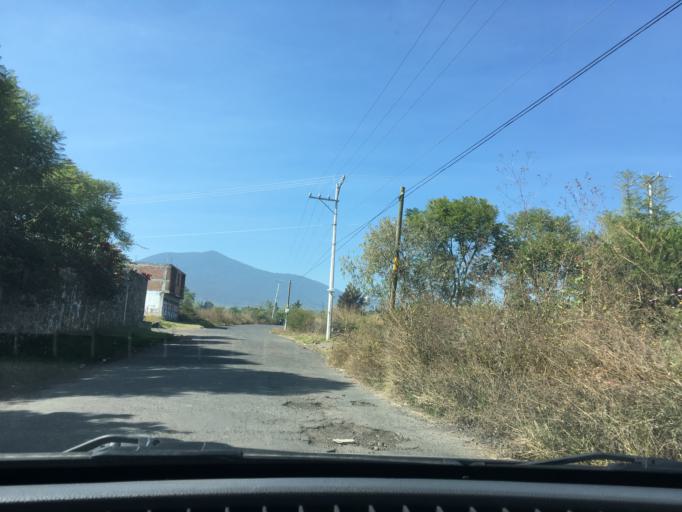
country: MX
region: Michoacan
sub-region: Morelia
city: La Mintzita (Piedra Dura)
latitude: 19.6488
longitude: -101.2903
